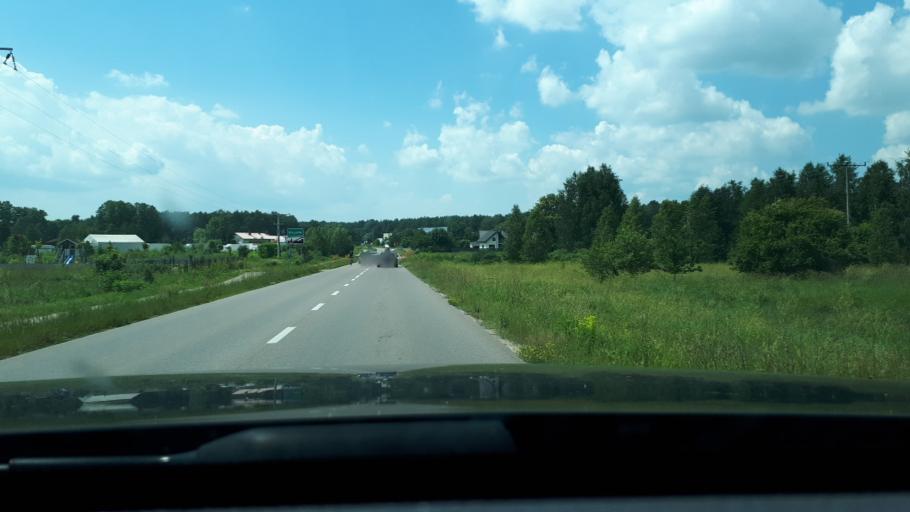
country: PL
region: Podlasie
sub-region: Powiat bialostocki
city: Choroszcz
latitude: 53.1311
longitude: 23.0530
